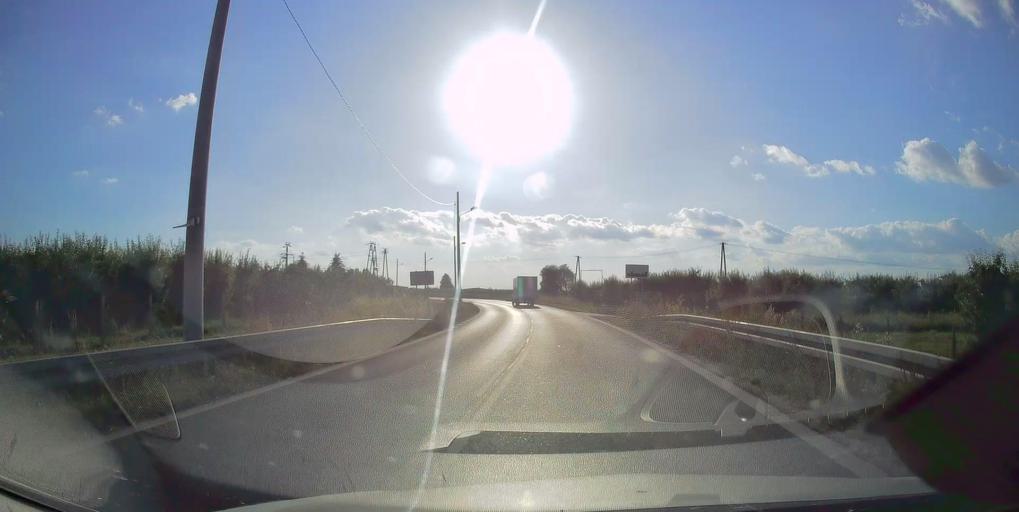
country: PL
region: Lodz Voivodeship
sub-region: Powiat rawski
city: Biala Rawska
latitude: 51.8074
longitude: 20.5654
